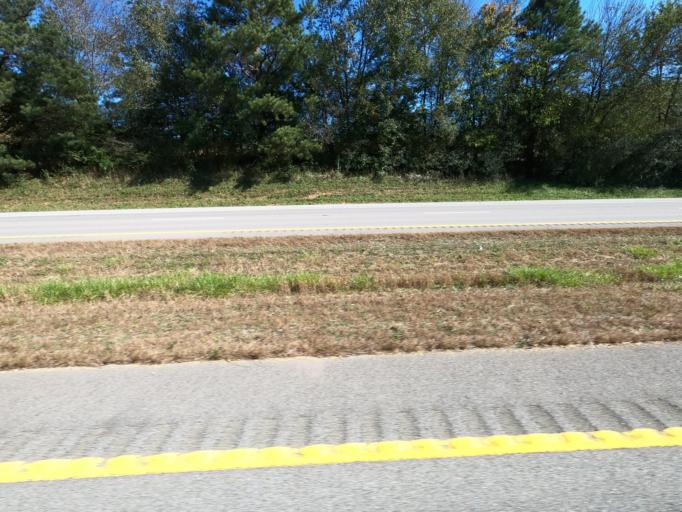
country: US
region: Tennessee
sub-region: Maury County
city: Mount Pleasant
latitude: 35.4186
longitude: -87.2822
